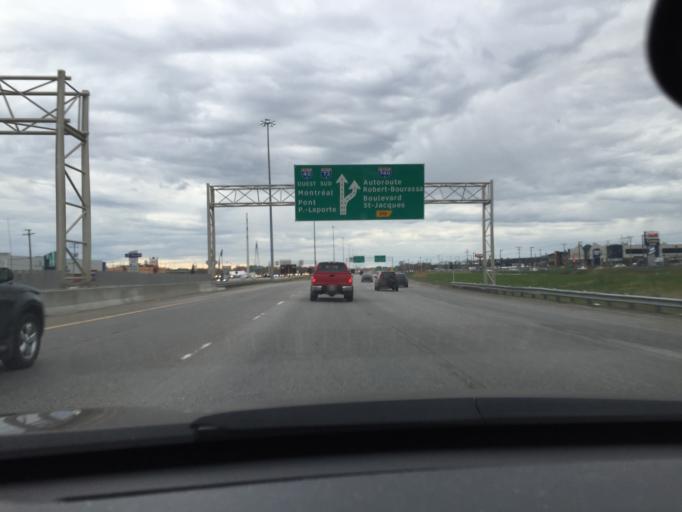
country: CA
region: Quebec
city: Quebec
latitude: 46.8291
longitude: -71.2833
